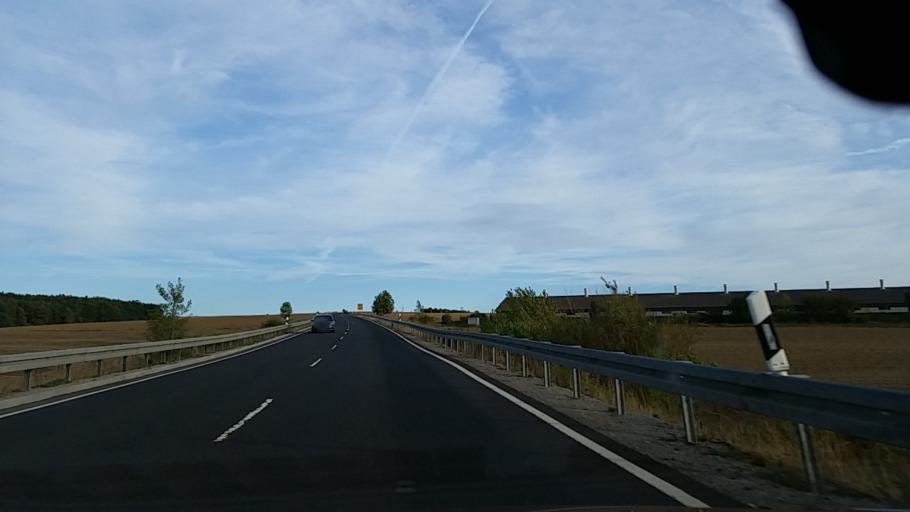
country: DE
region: Bavaria
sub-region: Regierungsbezirk Unterfranken
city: Mellrichstadt
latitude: 50.4307
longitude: 10.3294
